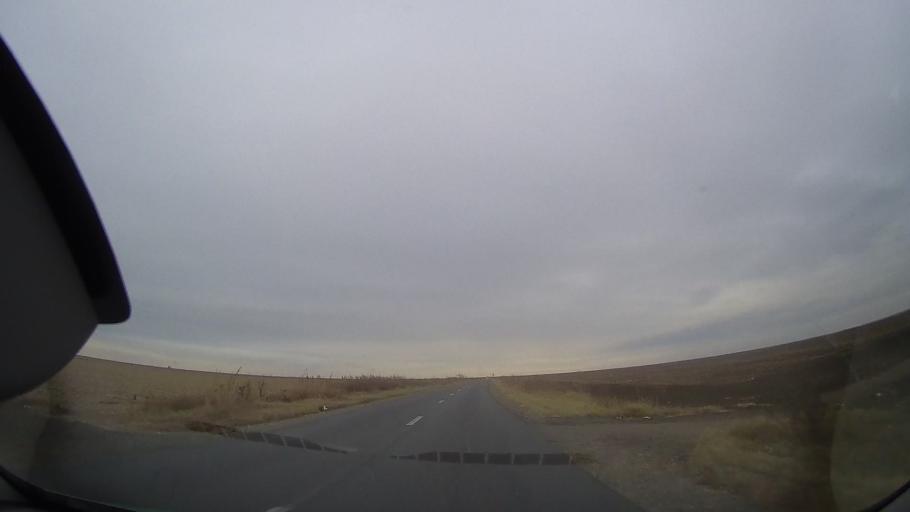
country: RO
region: Ialomita
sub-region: Oras Amara
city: Amara
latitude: 44.6447
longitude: 27.3005
